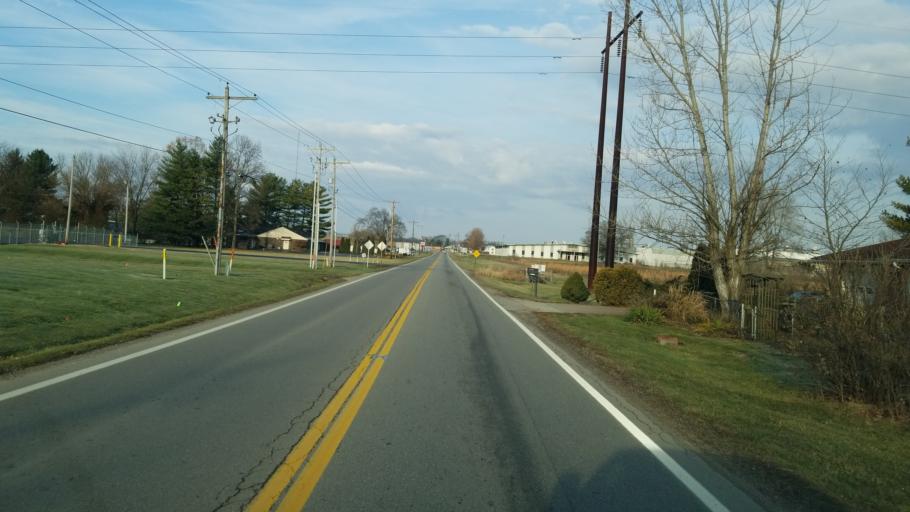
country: US
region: Ohio
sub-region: Ross County
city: Chillicothe
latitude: 39.3199
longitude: -82.9476
